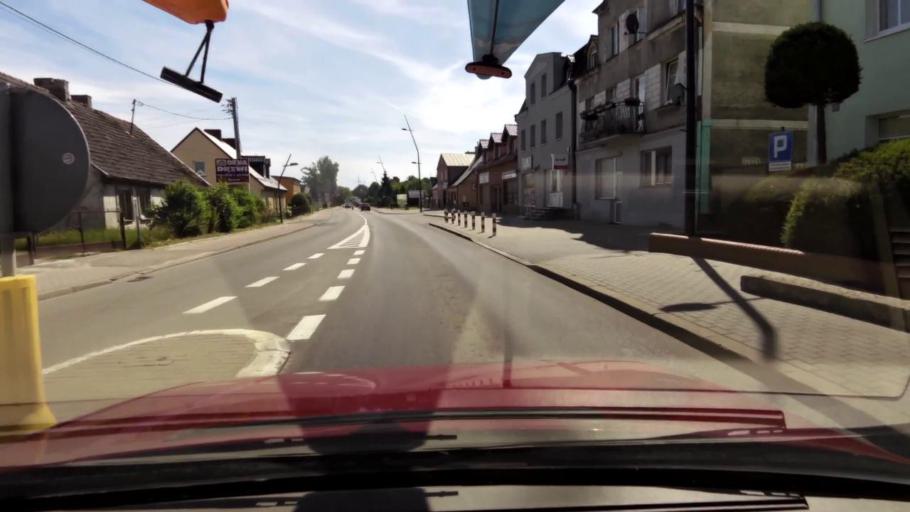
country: PL
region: Pomeranian Voivodeship
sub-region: Powiat slupski
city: Kobylnica
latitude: 54.4436
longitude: 17.0002
